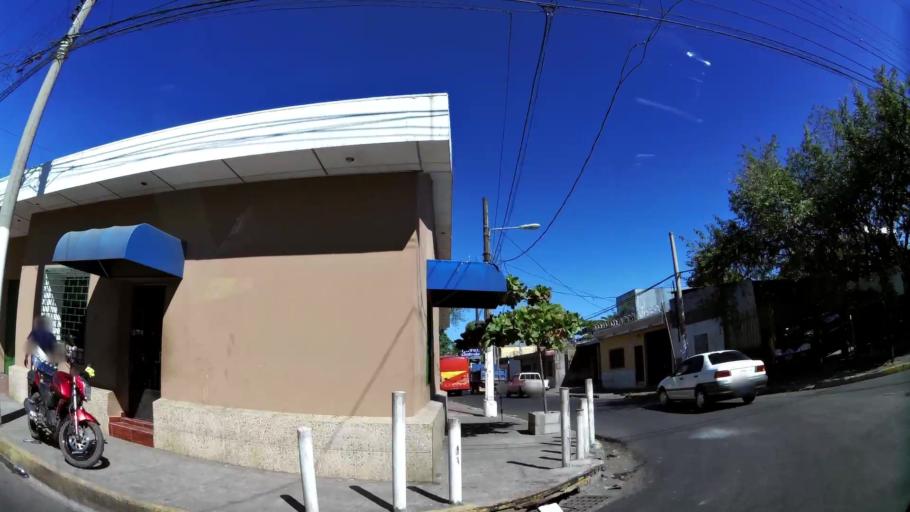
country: SV
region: San Miguel
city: San Miguel
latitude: 13.4834
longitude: -88.1703
